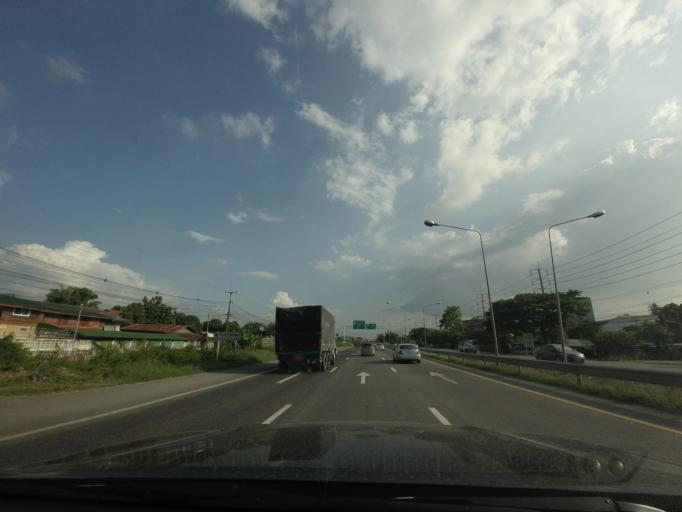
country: TH
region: Sara Buri
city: Saraburi
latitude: 14.5711
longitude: 100.9029
